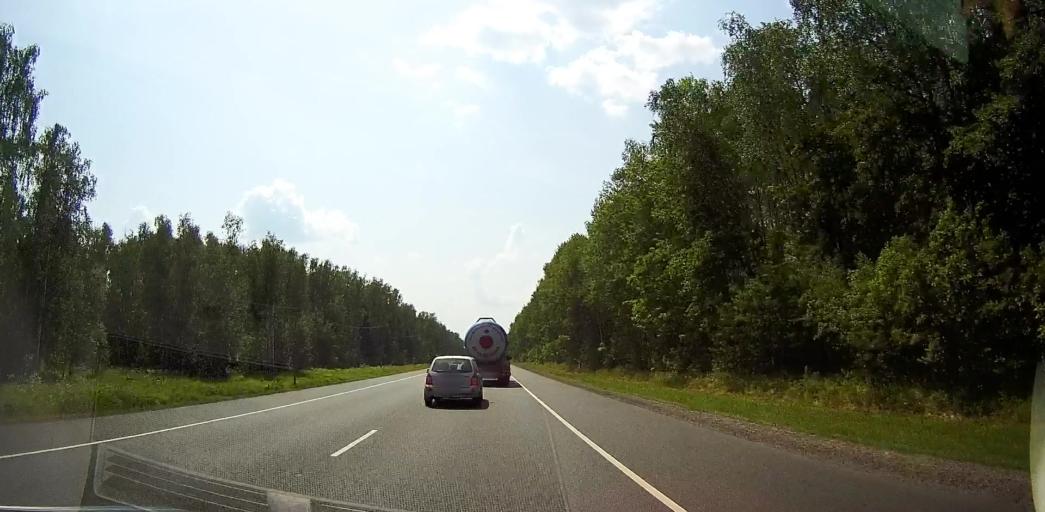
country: RU
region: Moskovskaya
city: Meshcherino
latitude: 55.2177
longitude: 38.3949
